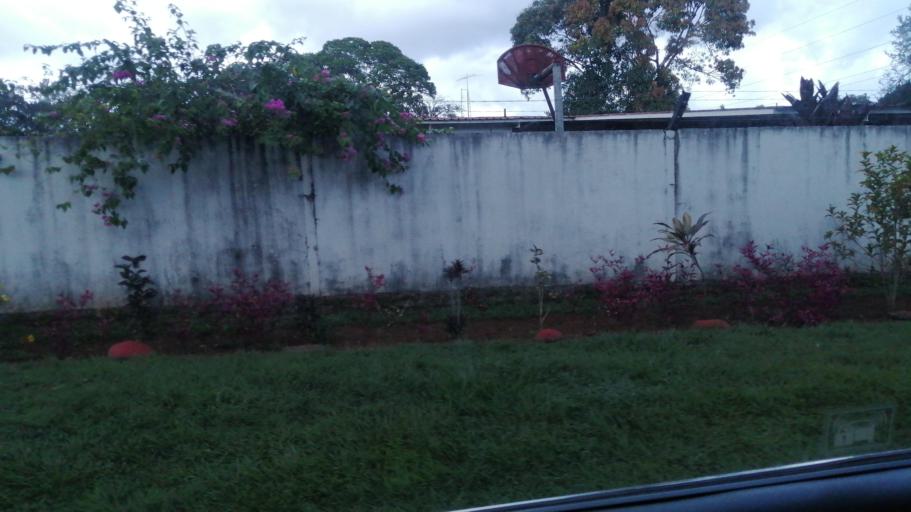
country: PA
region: Chiriqui
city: Mata del Nance
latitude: 8.4504
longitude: -82.4234
